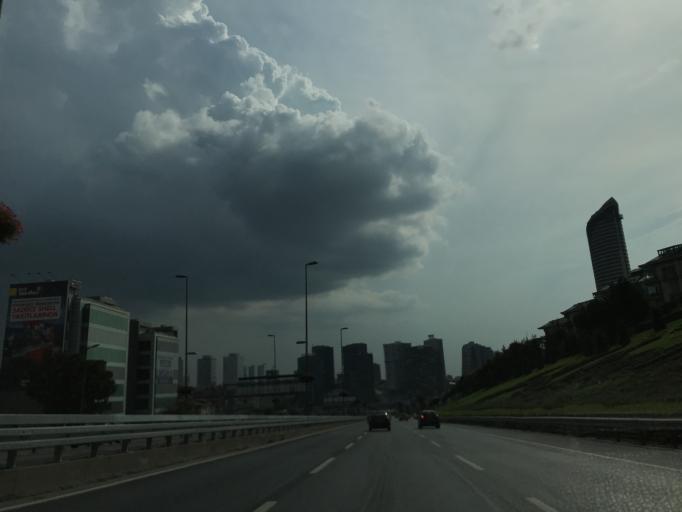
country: TR
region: Istanbul
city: UEskuedar
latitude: 41.0048
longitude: 29.0599
